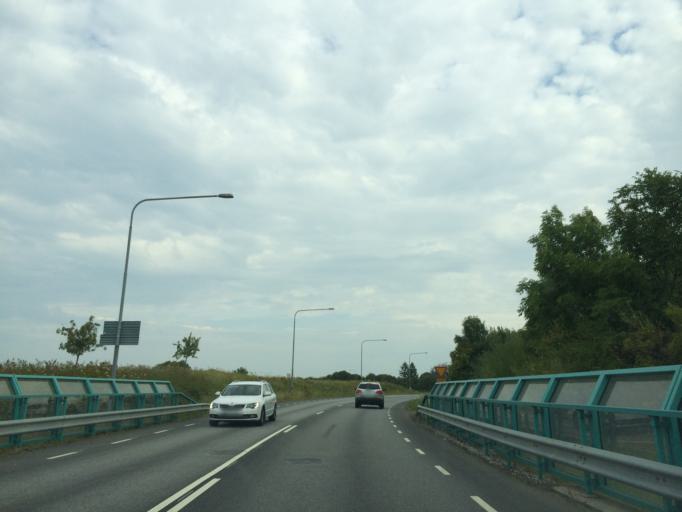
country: SE
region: Skane
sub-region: Burlovs Kommun
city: Arloev
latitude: 55.5898
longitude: 13.1049
